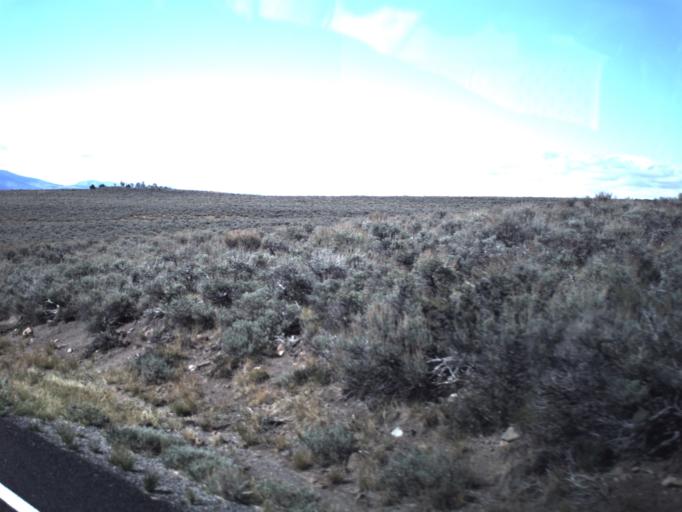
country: US
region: Utah
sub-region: Wayne County
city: Loa
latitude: 38.5107
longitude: -111.7918
